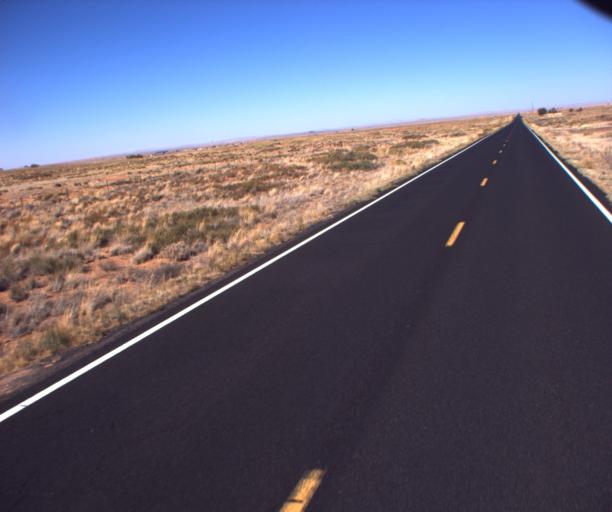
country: US
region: Arizona
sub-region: Navajo County
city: Dilkon
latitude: 35.4856
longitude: -110.4291
